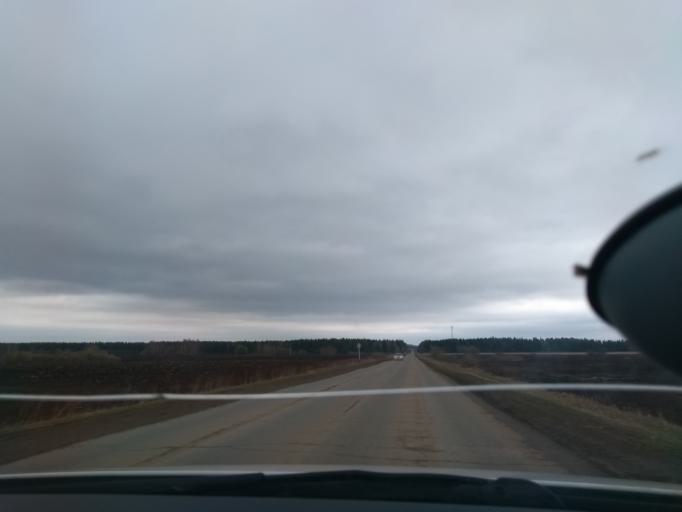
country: RU
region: Perm
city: Kungur
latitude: 57.3890
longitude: 56.8644
